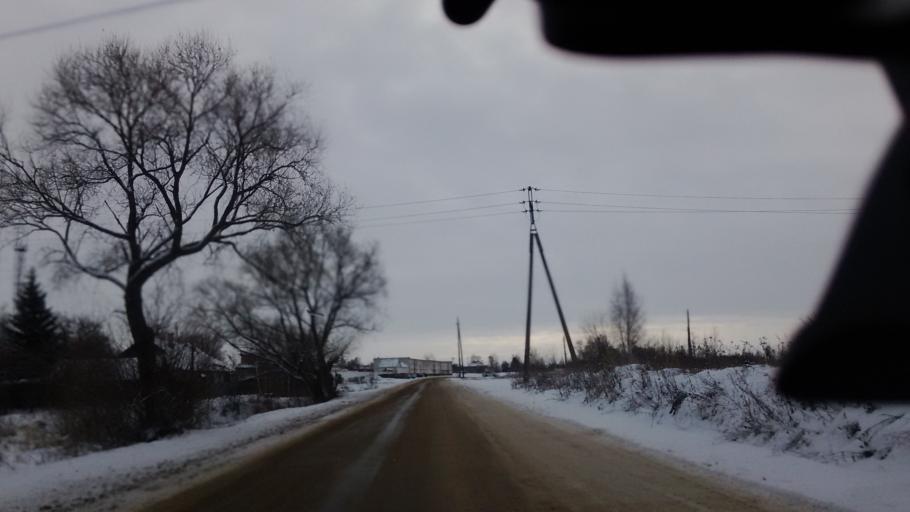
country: RU
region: Tula
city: Bogoroditsk
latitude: 53.7597
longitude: 38.1061
